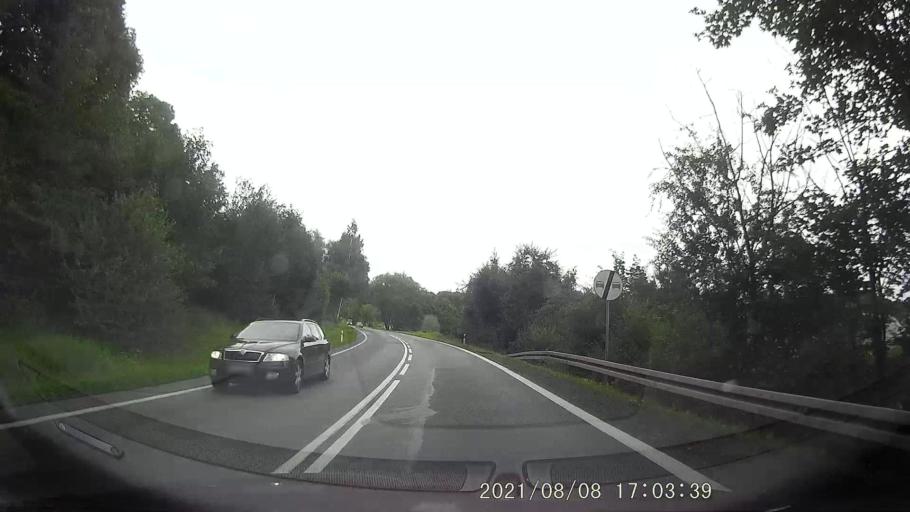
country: PL
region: Lower Silesian Voivodeship
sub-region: Powiat klodzki
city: Lewin Klodzki
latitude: 50.4064
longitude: 16.2884
